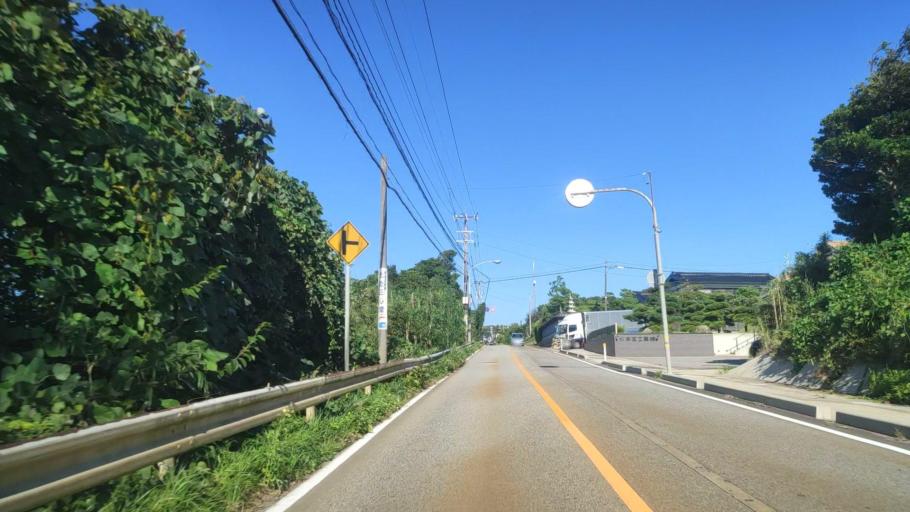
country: JP
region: Ishikawa
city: Hakui
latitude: 36.9246
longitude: 136.7637
